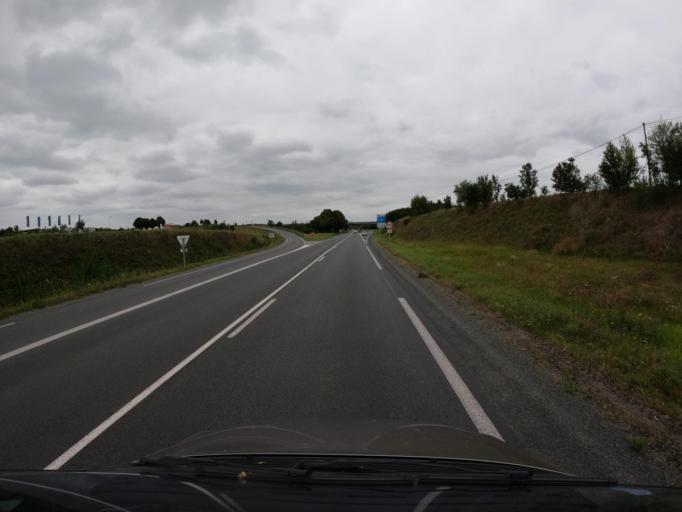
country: FR
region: Pays de la Loire
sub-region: Departement de la Vendee
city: Fontenay-le-Comte
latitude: 46.4468
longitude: -0.8103
